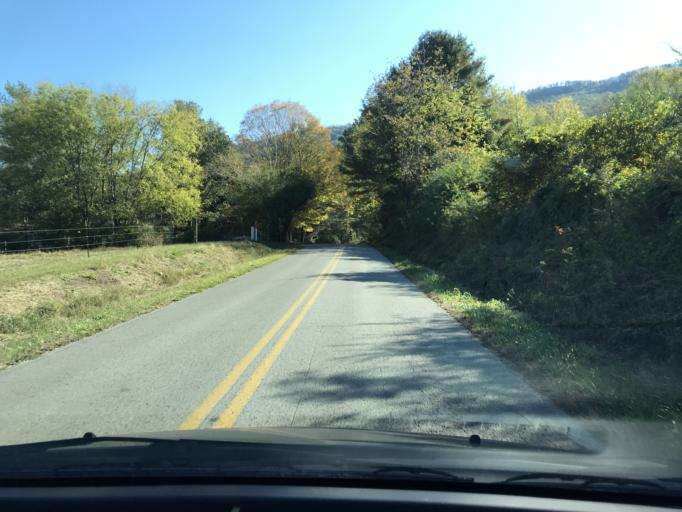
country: US
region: Georgia
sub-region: Dade County
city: Trenton
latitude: 34.8948
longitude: -85.4655
